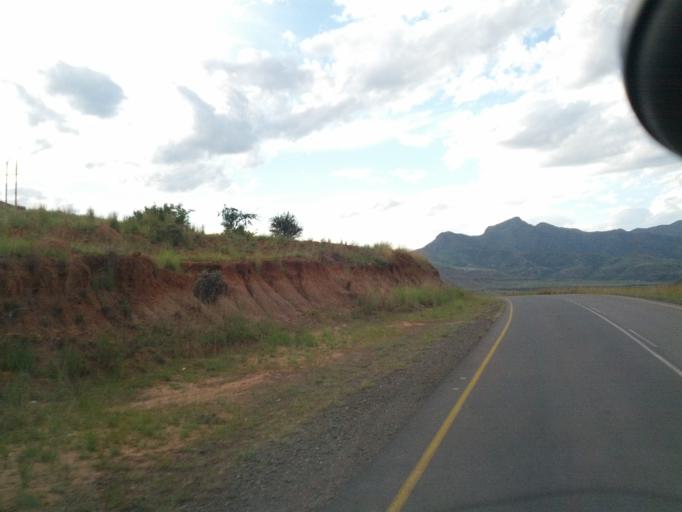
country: LS
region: Qacha's Nek
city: Qacha's Nek
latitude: -30.0839
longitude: 28.6326
